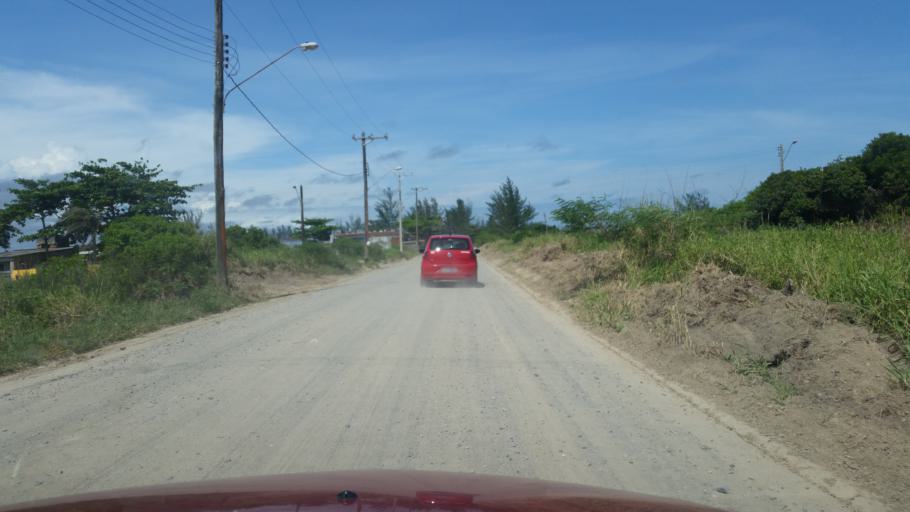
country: BR
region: Sao Paulo
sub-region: Iguape
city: Iguape
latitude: -24.6982
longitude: -47.4569
